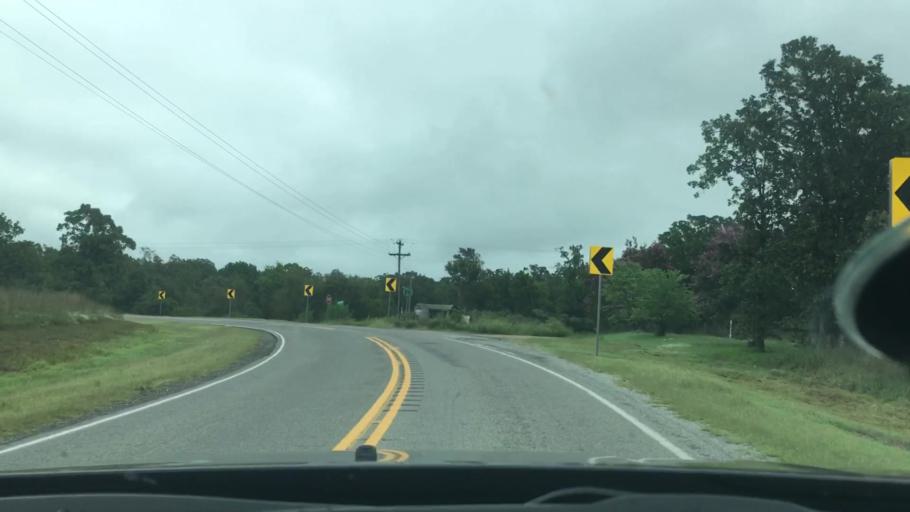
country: US
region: Oklahoma
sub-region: Sequoyah County
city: Vian
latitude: 35.6211
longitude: -94.9608
